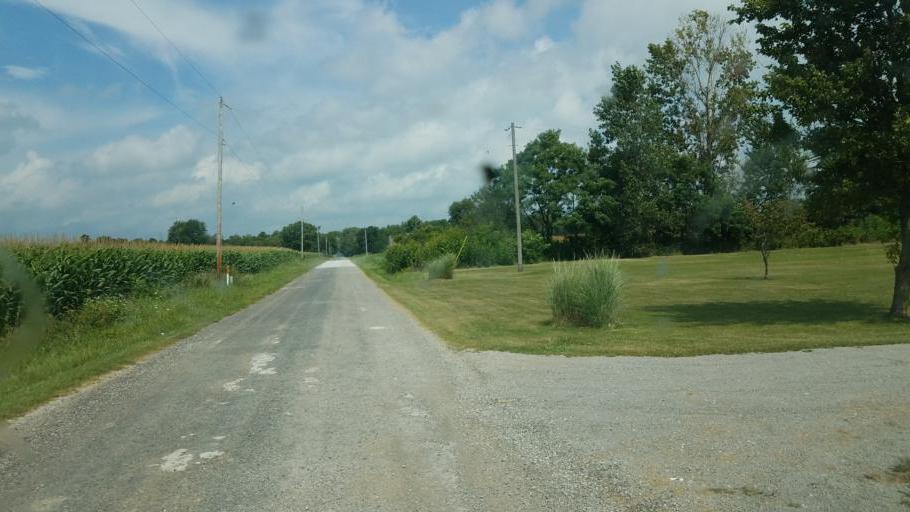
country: US
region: Ohio
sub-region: Morrow County
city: Mount Gilead
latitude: 40.6117
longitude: -82.7092
